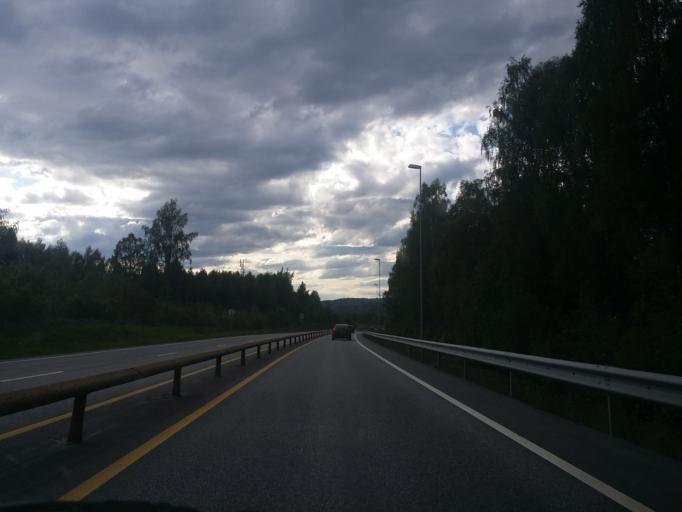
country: NO
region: Hedmark
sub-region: Hamar
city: Hamar
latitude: 60.7821
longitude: 11.1368
